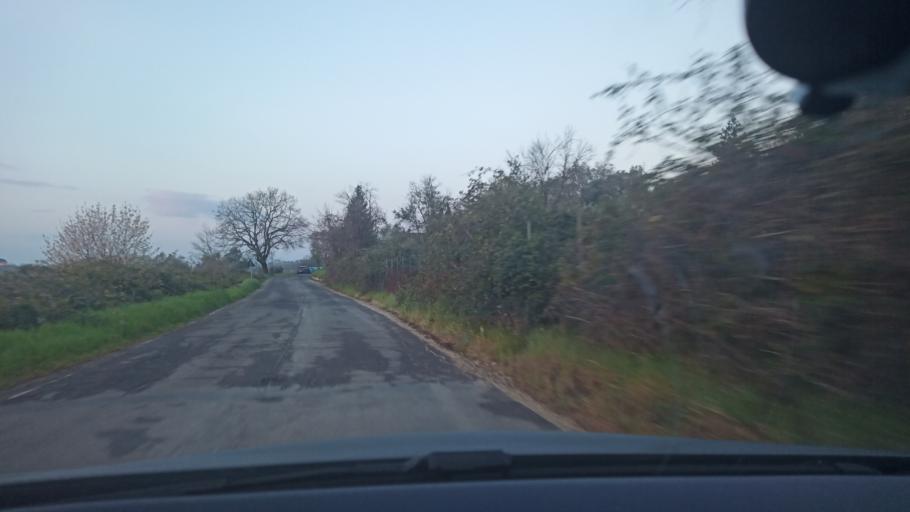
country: IT
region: Latium
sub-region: Provincia di Rieti
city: Vacone
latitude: 42.3657
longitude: 12.6584
